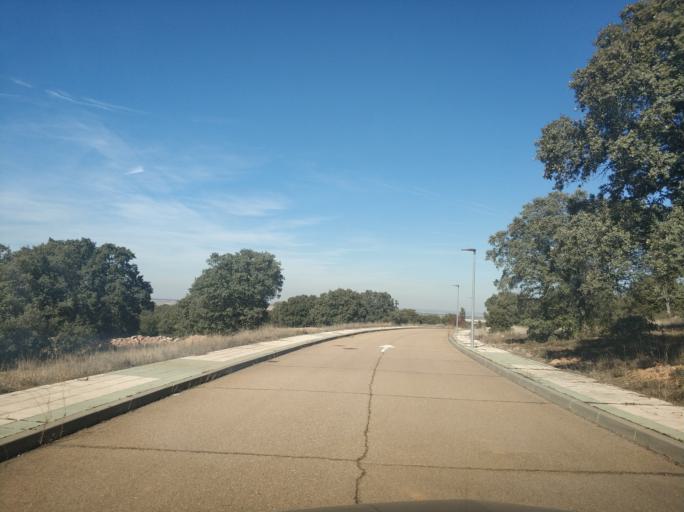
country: ES
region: Castille and Leon
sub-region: Provincia de Salamanca
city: Doninos de Salamanca
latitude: 40.9331
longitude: -5.7448
